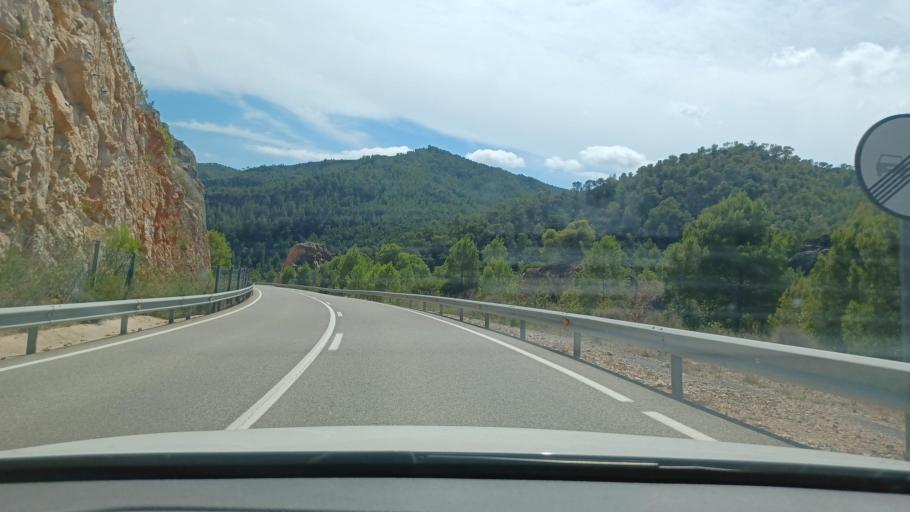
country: ES
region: Catalonia
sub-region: Provincia de Tarragona
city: Benifallet
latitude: 40.9587
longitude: 0.4451
